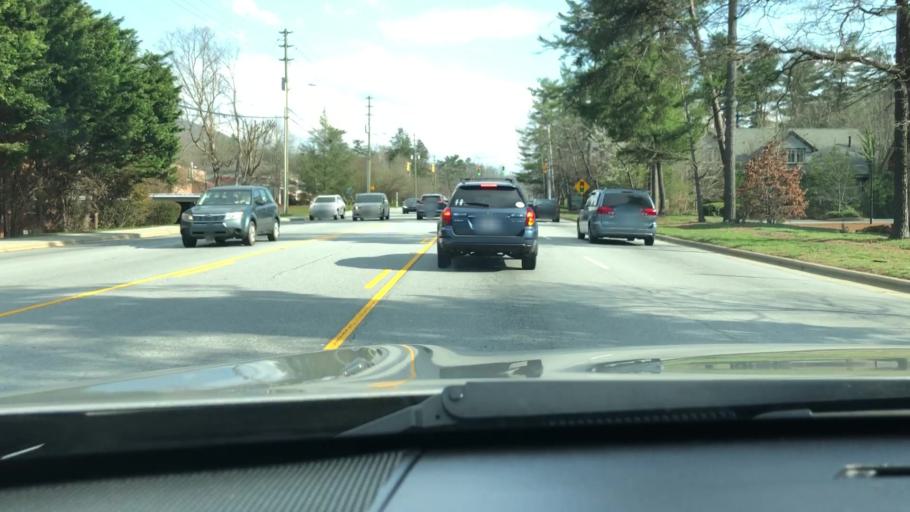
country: US
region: North Carolina
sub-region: Buncombe County
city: Biltmore Forest
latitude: 35.5373
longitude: -82.5298
